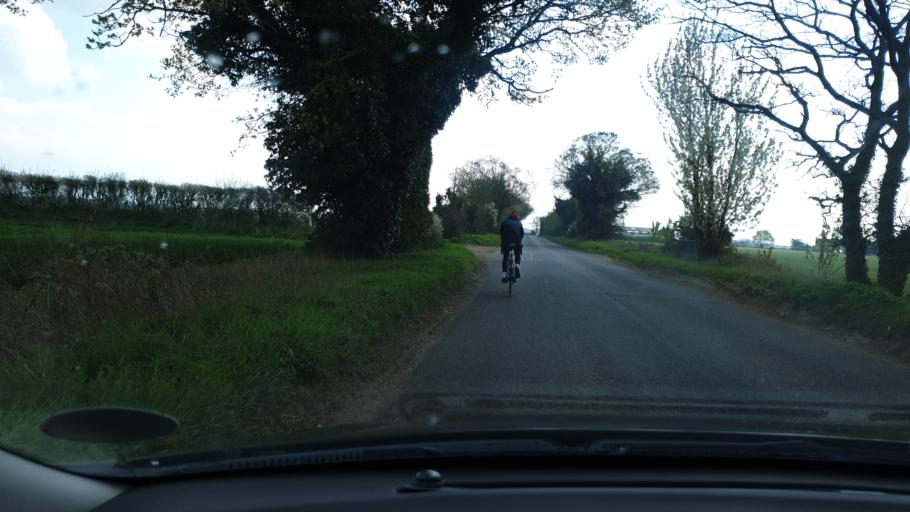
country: GB
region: England
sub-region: Essex
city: Great Bentley
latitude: 51.8553
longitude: 1.0400
